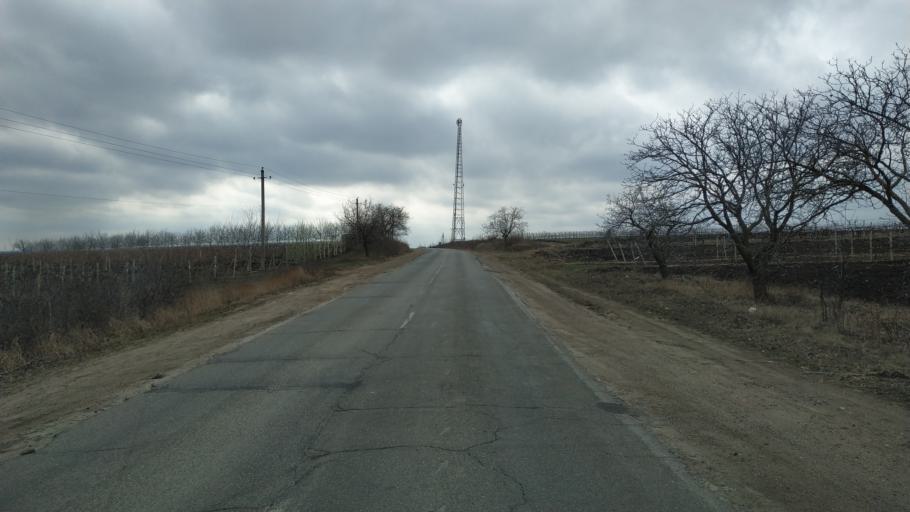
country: MD
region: Laloveni
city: Ialoveni
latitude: 46.8906
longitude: 28.7687
